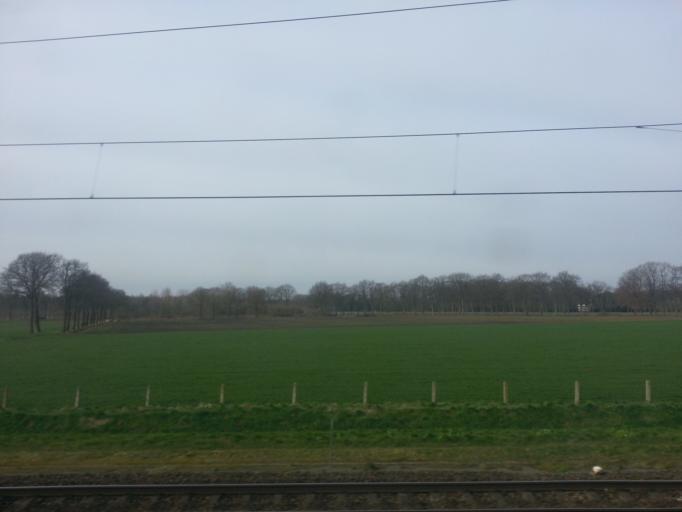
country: NL
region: North Brabant
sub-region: Gemeente Boxtel
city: Boxtel
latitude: 51.5637
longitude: 5.3399
